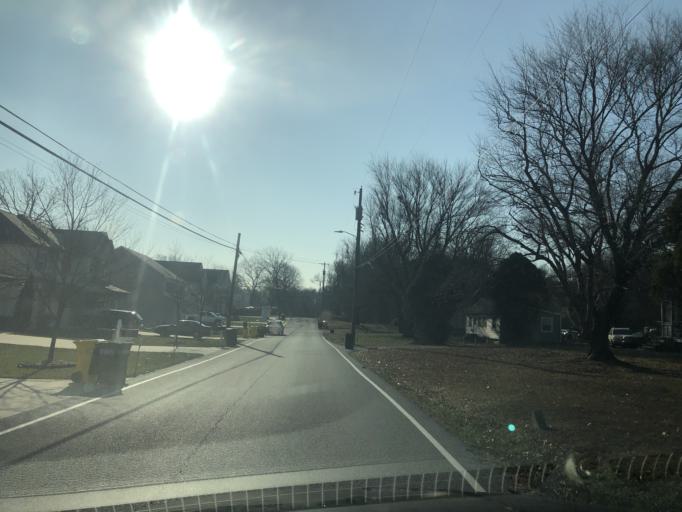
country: US
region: Maryland
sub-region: Anne Arundel County
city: Odenton
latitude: 39.0739
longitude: -76.7081
